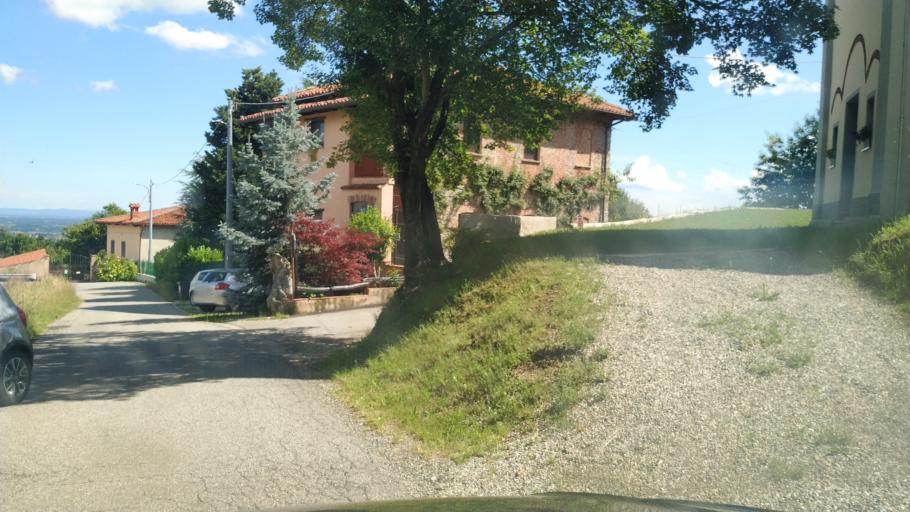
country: IT
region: Piedmont
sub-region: Provincia di Torino
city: Cintano
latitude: 45.4189
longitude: 7.7077
